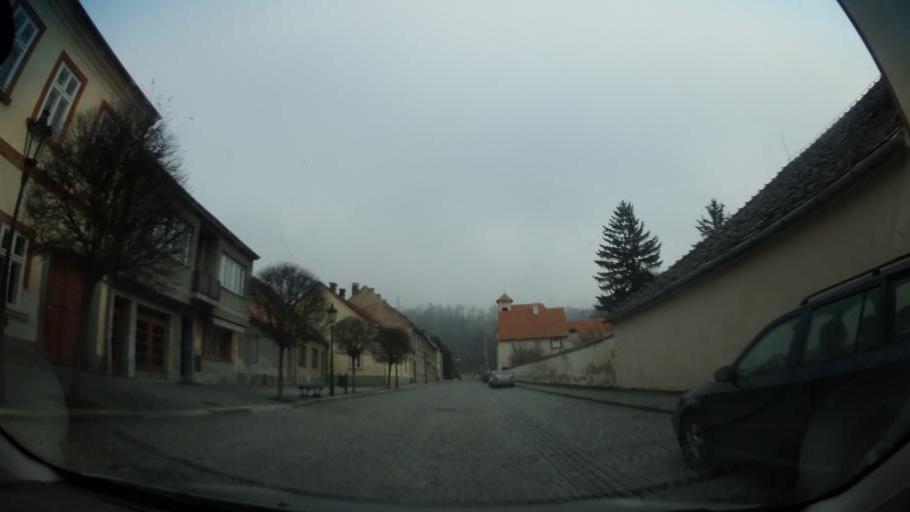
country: CZ
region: Vysocina
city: Namest' nad Oslavou
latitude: 49.2078
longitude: 16.1578
